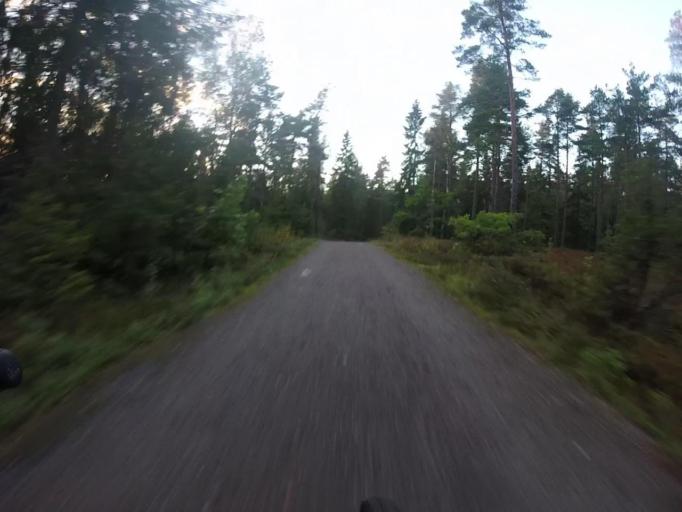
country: SE
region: Vaestra Goetaland
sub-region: Trollhattan
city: Trollhattan
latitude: 58.2976
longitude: 12.2673
